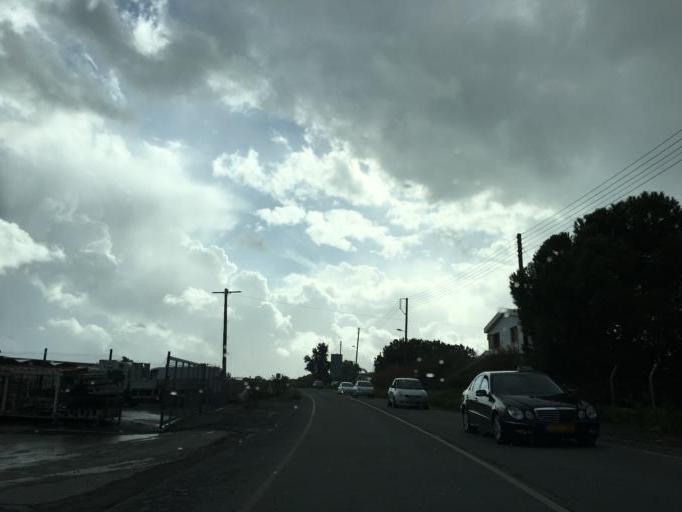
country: CY
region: Limassol
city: Erimi
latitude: 34.6744
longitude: 32.9149
